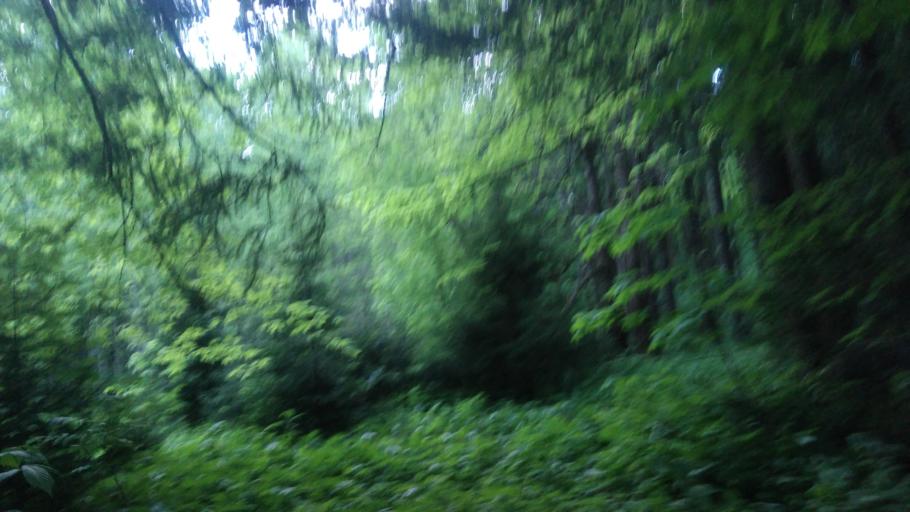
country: RU
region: Perm
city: Ferma
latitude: 57.9665
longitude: 56.3411
